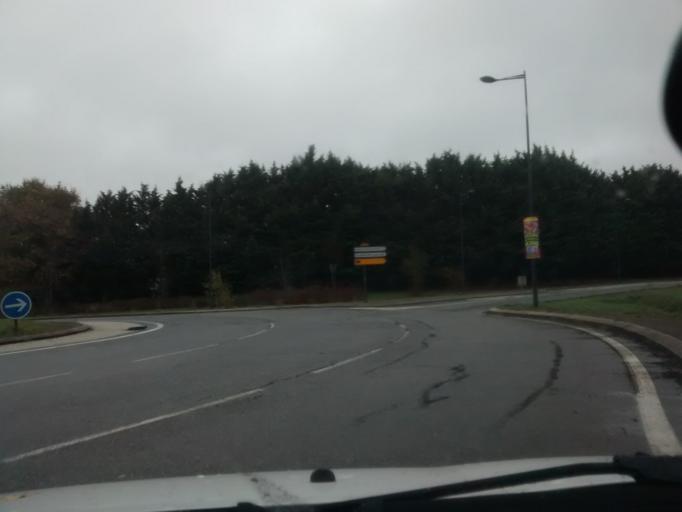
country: FR
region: Brittany
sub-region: Departement d'Ille-et-Vilaine
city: Chantepie
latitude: 48.0796
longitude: -1.6045
